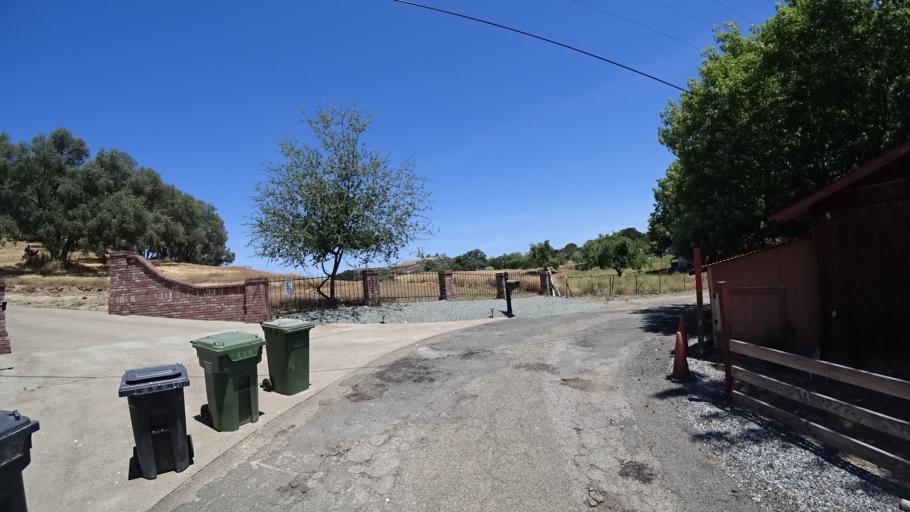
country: US
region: California
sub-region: Calaveras County
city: Valley Springs
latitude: 38.1851
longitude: -120.8922
